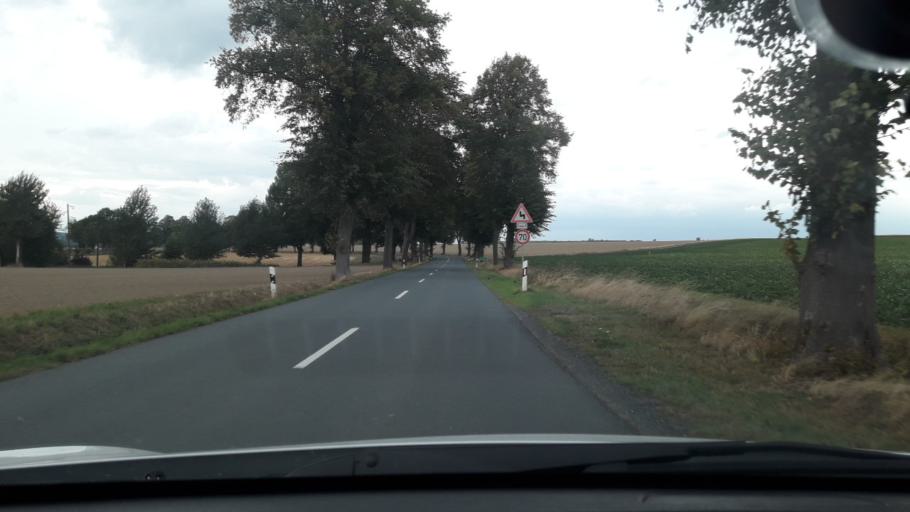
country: DE
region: Lower Saxony
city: Gielde
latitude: 52.0523
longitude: 10.4753
